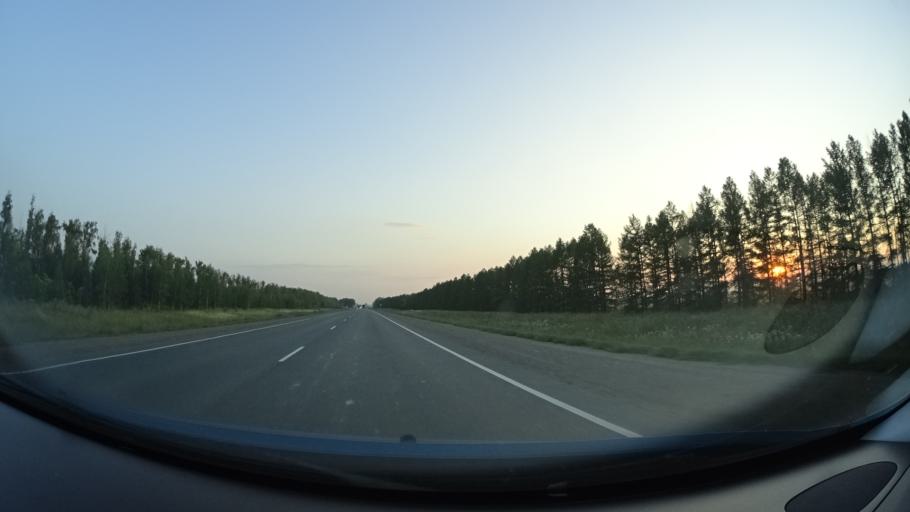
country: RU
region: Samara
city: Sukhodol
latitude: 53.8533
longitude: 51.1521
